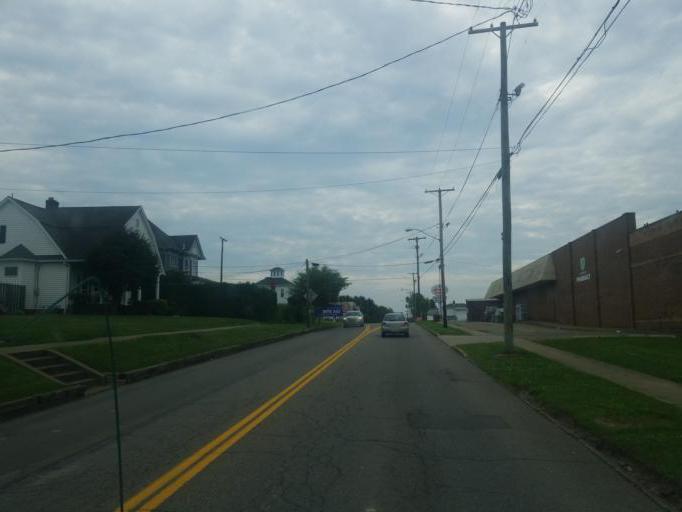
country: US
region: Ohio
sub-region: Carroll County
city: Carrollton
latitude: 40.5759
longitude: -81.0921
